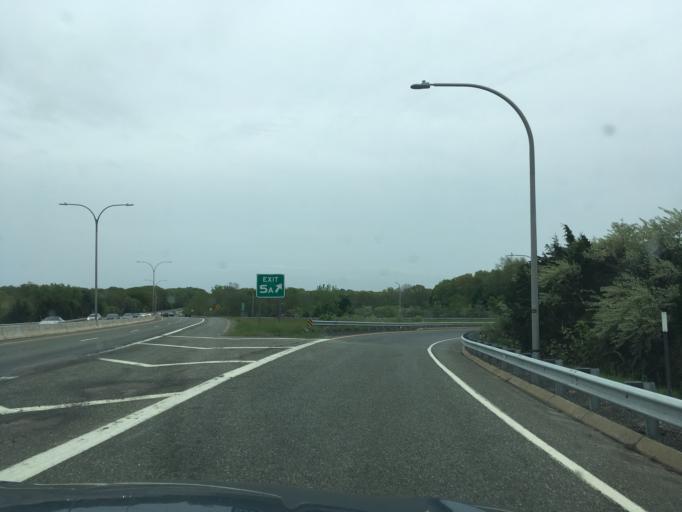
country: US
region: Rhode Island
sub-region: Washington County
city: Exeter
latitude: 41.5807
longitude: -71.5031
